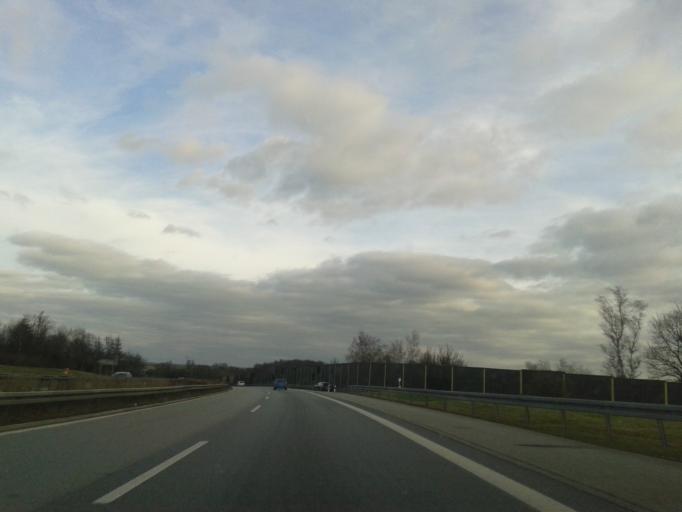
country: DE
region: Saxony
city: Bautzen
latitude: 51.1885
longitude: 14.4112
